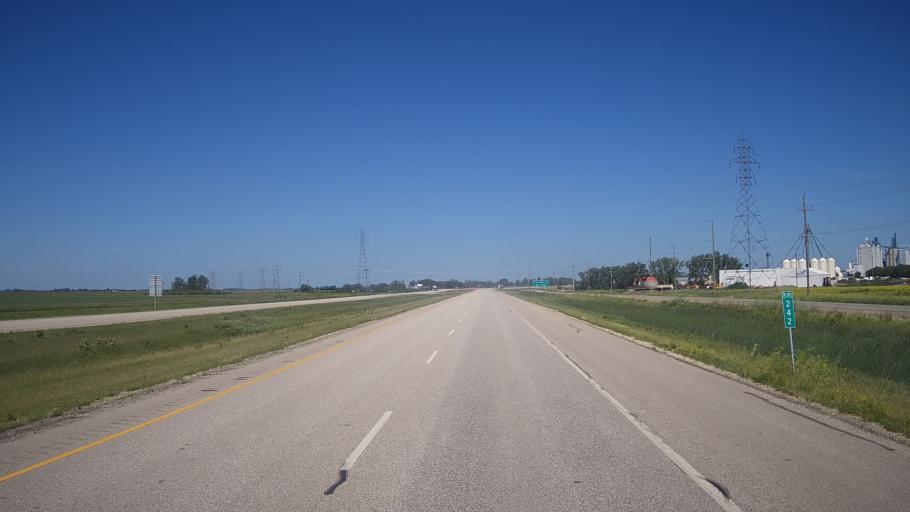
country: CA
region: Manitoba
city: Portage la Prairie
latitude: 49.9593
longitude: -98.3421
